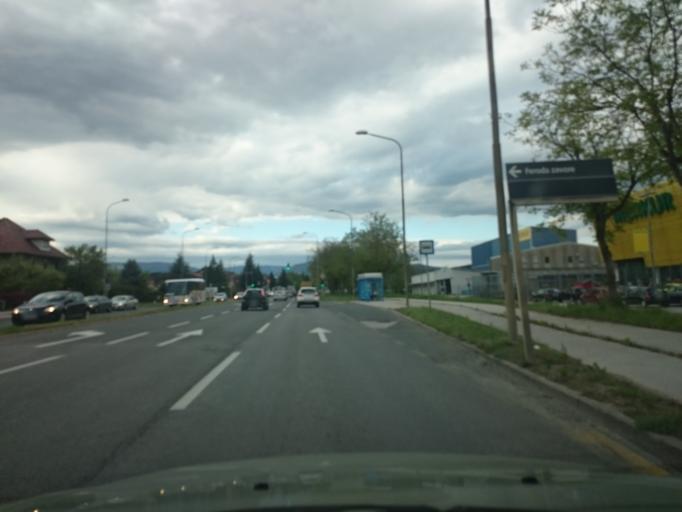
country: SI
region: Celje
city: Trnovlje pri Celju
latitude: 46.2495
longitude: 15.2802
